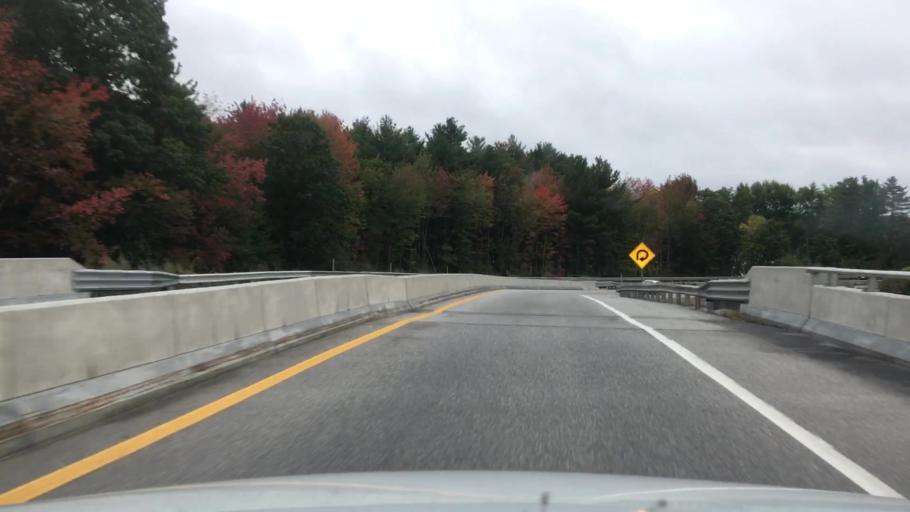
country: US
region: Maine
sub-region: Cumberland County
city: South Portland Gardens
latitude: 43.6806
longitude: -70.3248
